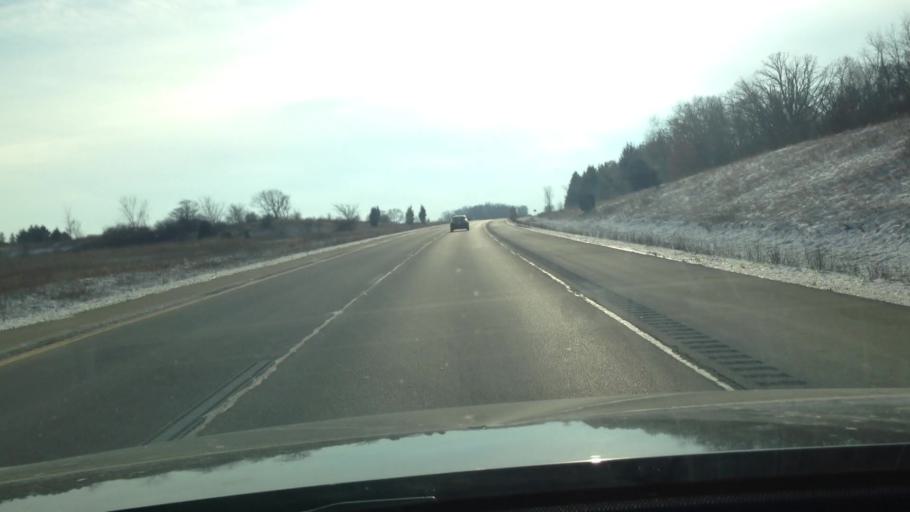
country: US
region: Wisconsin
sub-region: Walworth County
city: East Troy
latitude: 42.7582
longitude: -88.4346
